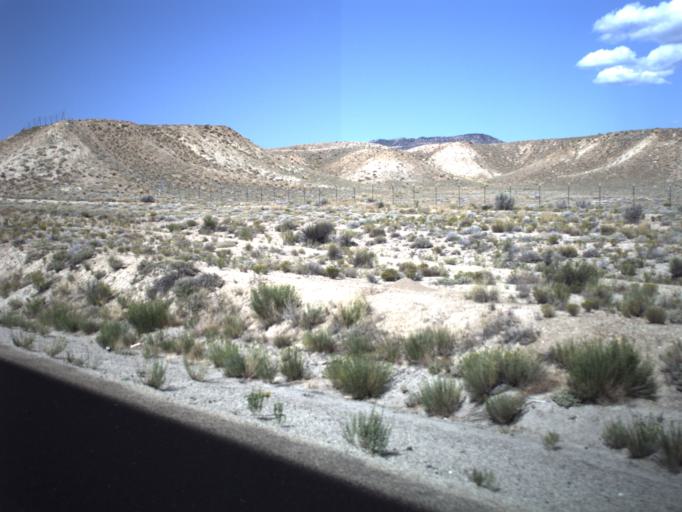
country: US
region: Utah
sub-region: Emery County
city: Ferron
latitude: 38.9671
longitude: -111.1878
